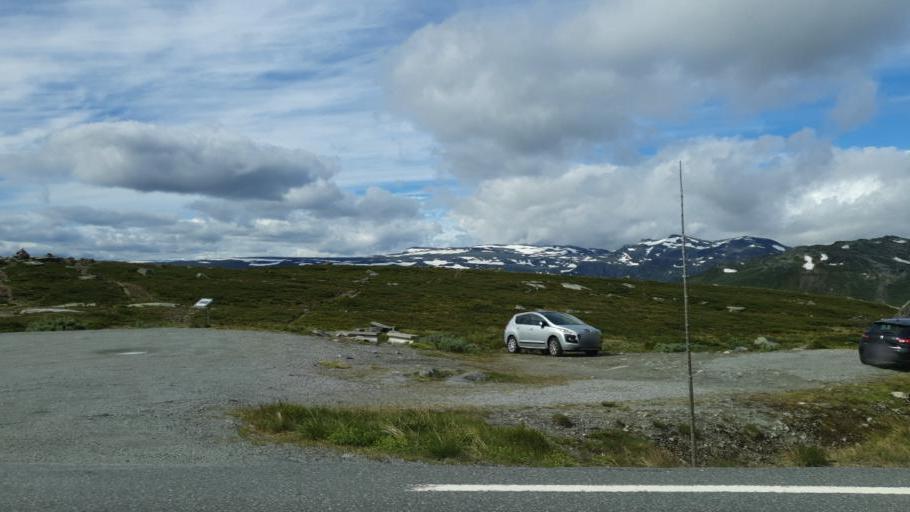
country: NO
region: Oppland
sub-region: Vestre Slidre
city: Slidre
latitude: 61.2840
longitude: 8.8297
